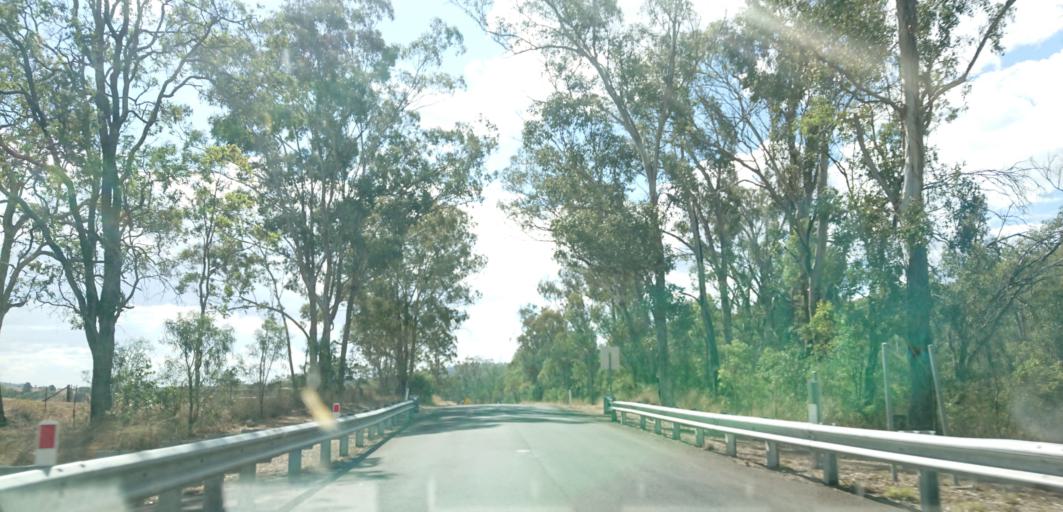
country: AU
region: Queensland
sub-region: Toowoomba
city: Top Camp
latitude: -27.7987
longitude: 152.1046
